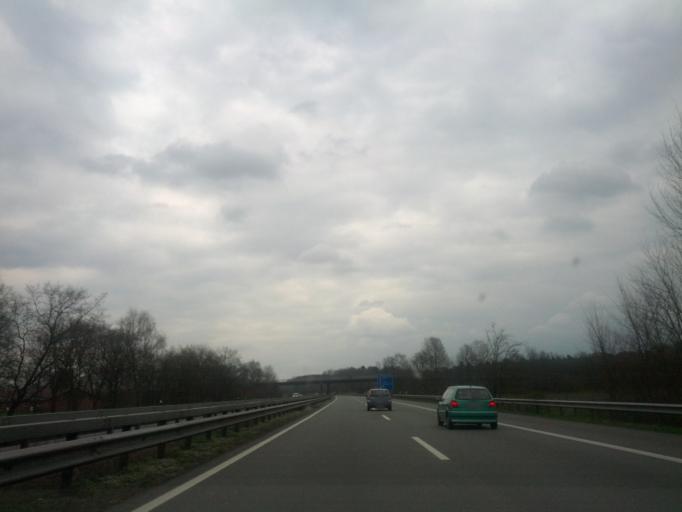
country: DE
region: Lower Saxony
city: Hude
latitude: 53.0591
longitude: 8.4408
